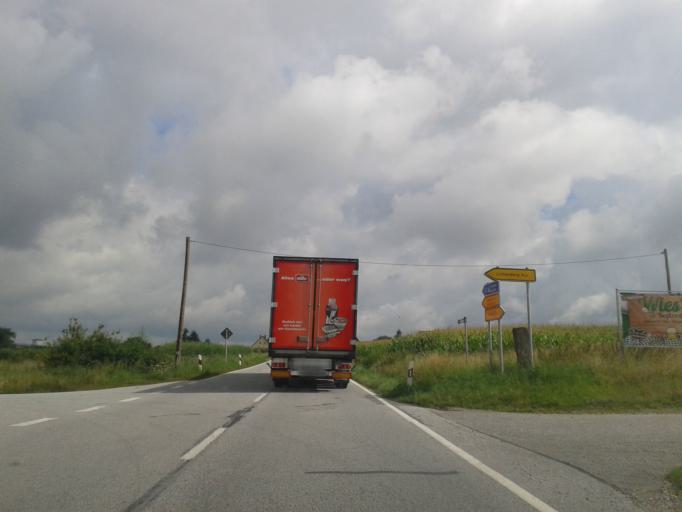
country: DE
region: Saxony
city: Lichtenberg
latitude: 51.1485
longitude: 13.9610
